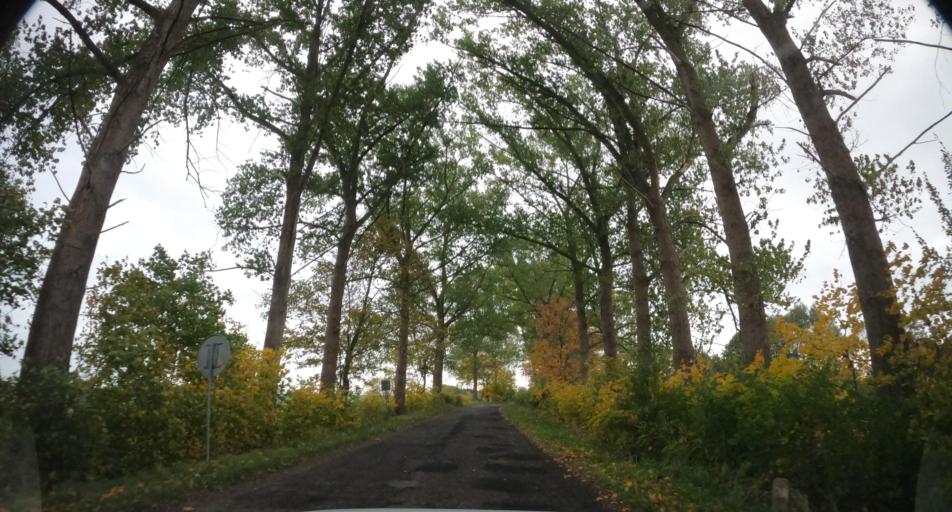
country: PL
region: West Pomeranian Voivodeship
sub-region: Powiat kamienski
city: Wolin
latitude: 53.8604
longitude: 14.6011
